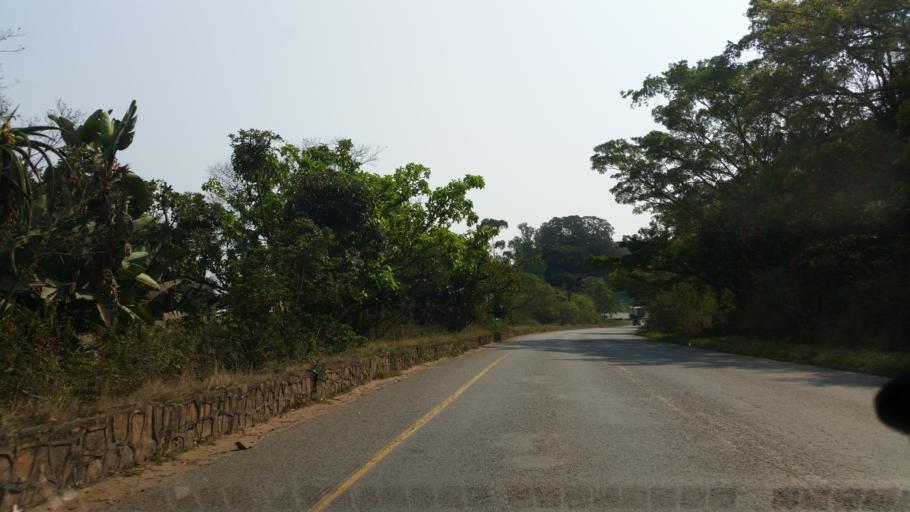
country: ZA
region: KwaZulu-Natal
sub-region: eThekwini Metropolitan Municipality
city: Mpumalanga
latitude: -29.7464
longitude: 30.6643
